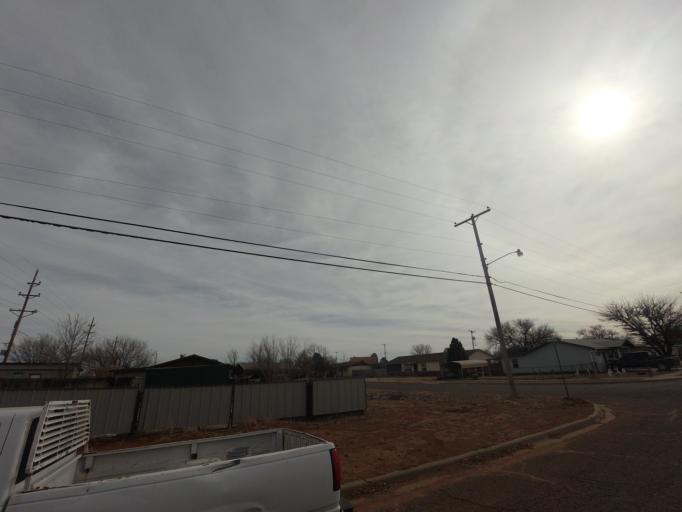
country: US
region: New Mexico
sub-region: Curry County
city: Clovis
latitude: 34.4117
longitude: -103.2448
